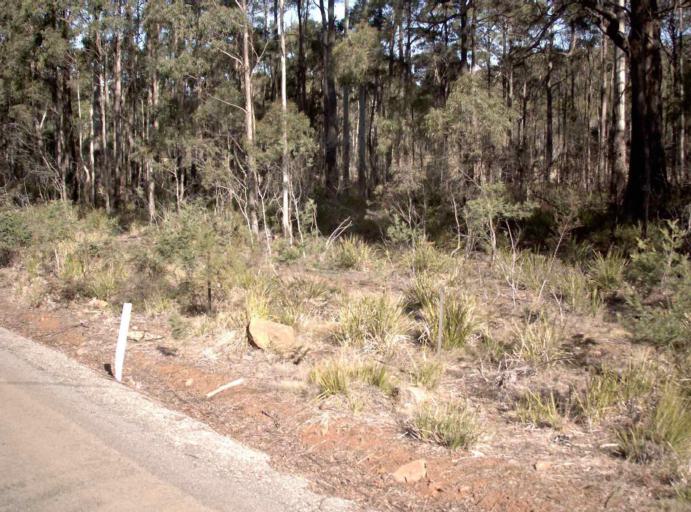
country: AU
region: Tasmania
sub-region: Launceston
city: Mayfield
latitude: -41.3179
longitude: 147.2085
